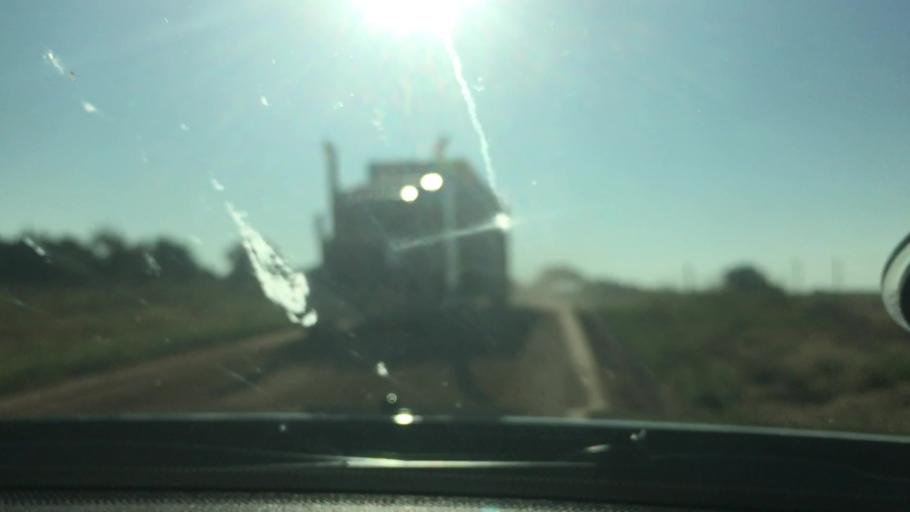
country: US
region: Oklahoma
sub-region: Murray County
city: Sulphur
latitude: 34.4194
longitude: -96.7845
